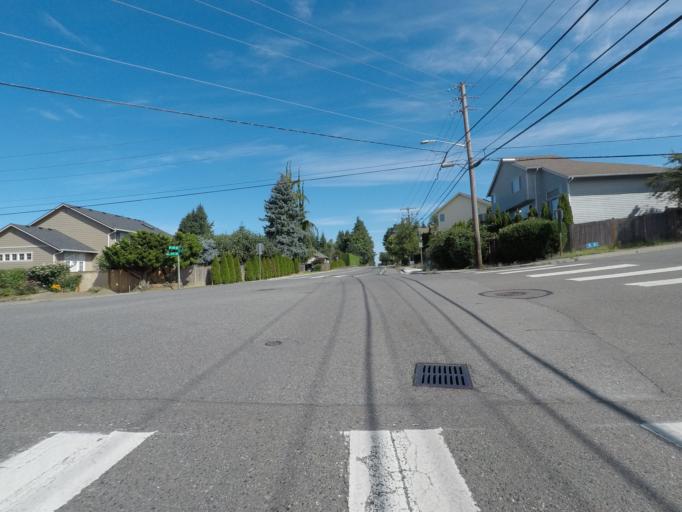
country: US
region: Washington
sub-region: King County
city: Inglewood-Finn Hill
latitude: 47.7115
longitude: -122.2296
